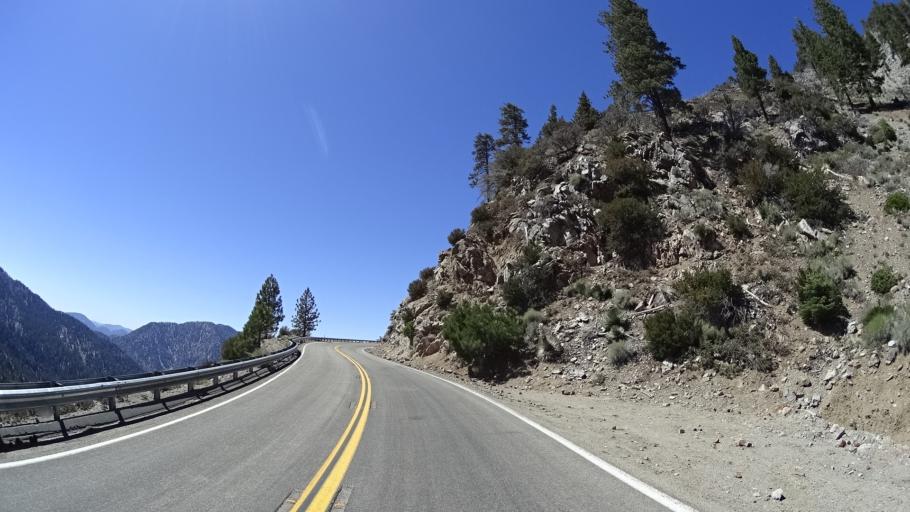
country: US
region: California
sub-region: San Bernardino County
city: Wrightwood
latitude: 34.3544
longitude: -117.8086
